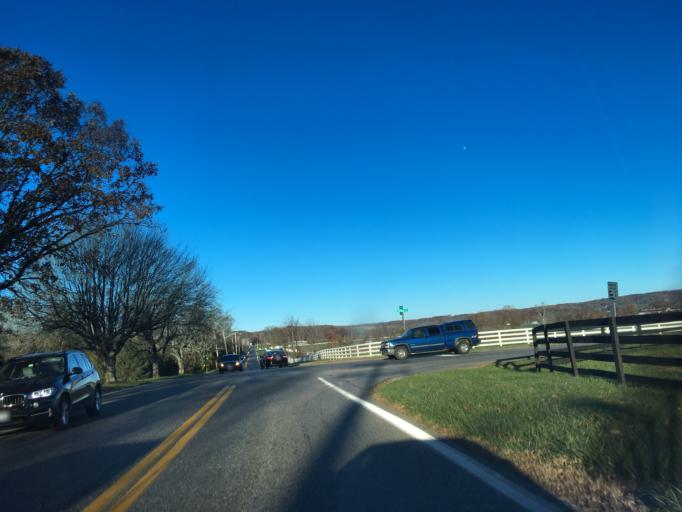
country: US
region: Maryland
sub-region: Baltimore County
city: Owings Mills
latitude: 39.4767
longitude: -76.7648
